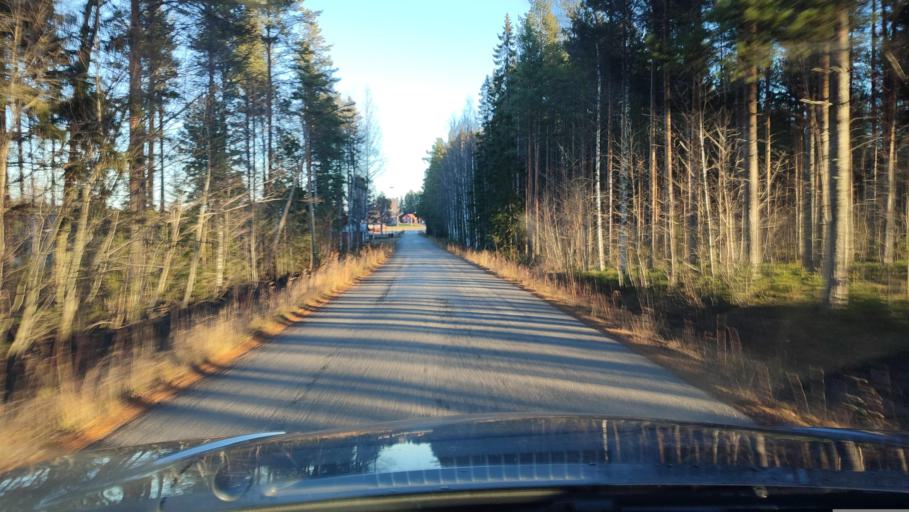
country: SE
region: Vaesterbotten
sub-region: Skelleftea Kommun
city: Soedra Bergsbyn
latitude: 64.6303
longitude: 21.0578
